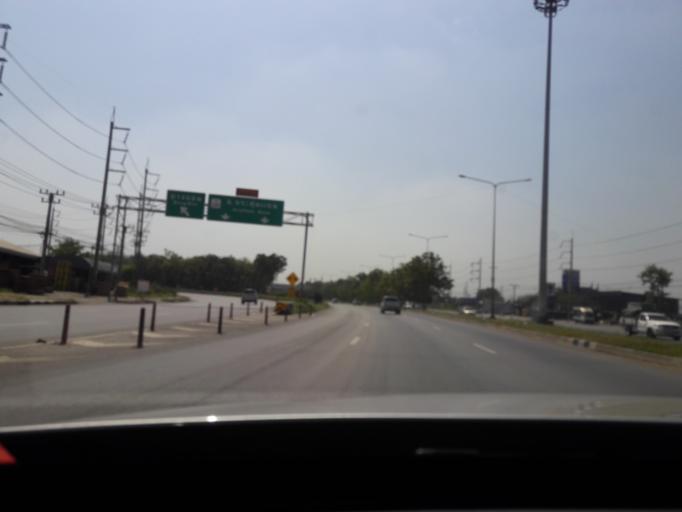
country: TH
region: Samut Sakhon
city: Krathum Baen
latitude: 13.6480
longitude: 100.3007
